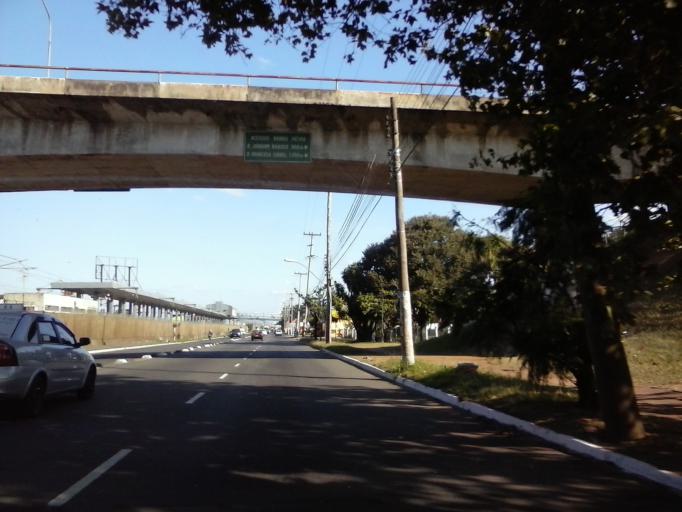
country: BR
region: Rio Grande do Sul
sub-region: Canoas
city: Canoas
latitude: -29.9360
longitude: -51.1777
